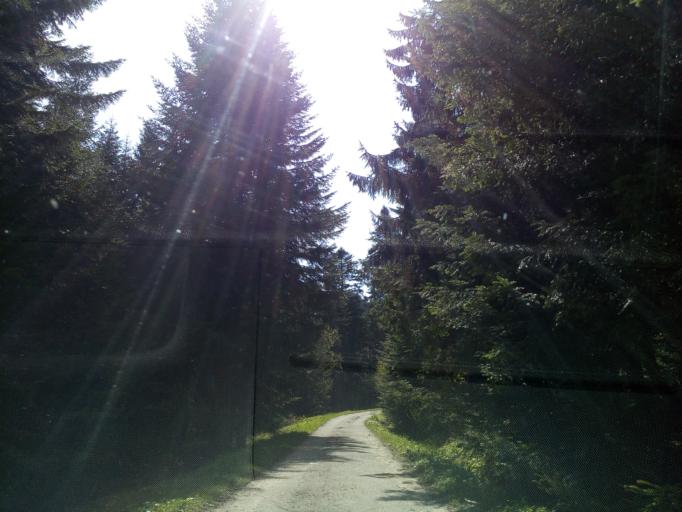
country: PL
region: Lesser Poland Voivodeship
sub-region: Powiat nowosadecki
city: Labowa
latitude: 49.4680
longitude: 20.8572
